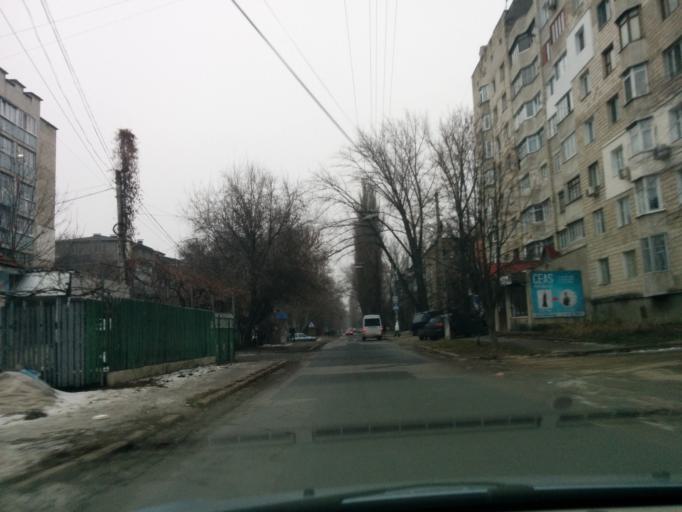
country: MD
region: Chisinau
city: Chisinau
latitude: 46.9971
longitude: 28.8647
